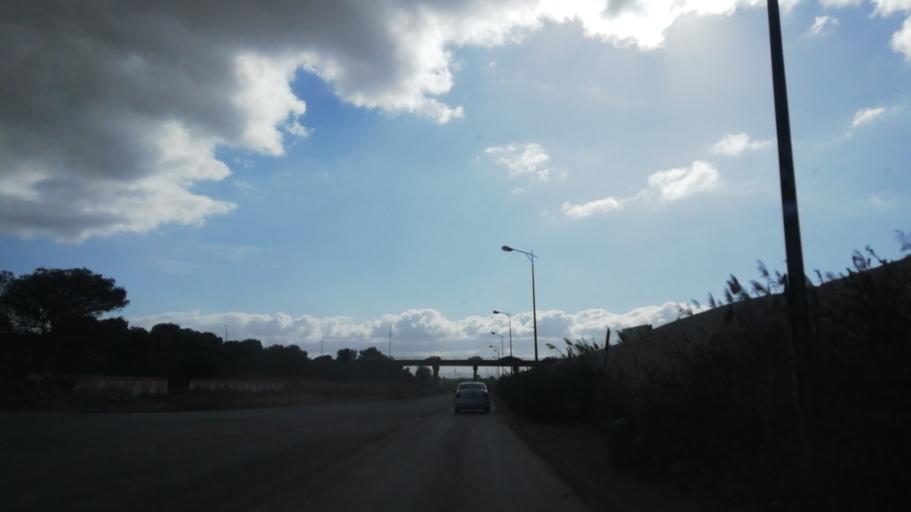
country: DZ
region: Oran
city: Es Senia
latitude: 35.6253
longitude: -0.5901
